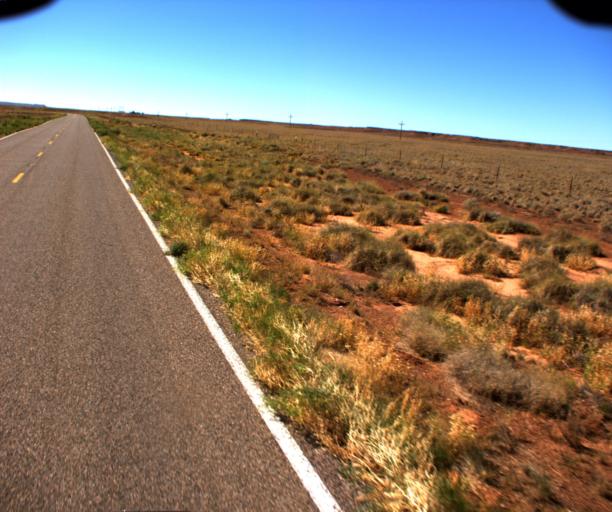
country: US
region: Arizona
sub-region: Coconino County
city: LeChee
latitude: 35.1659
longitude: -110.9139
